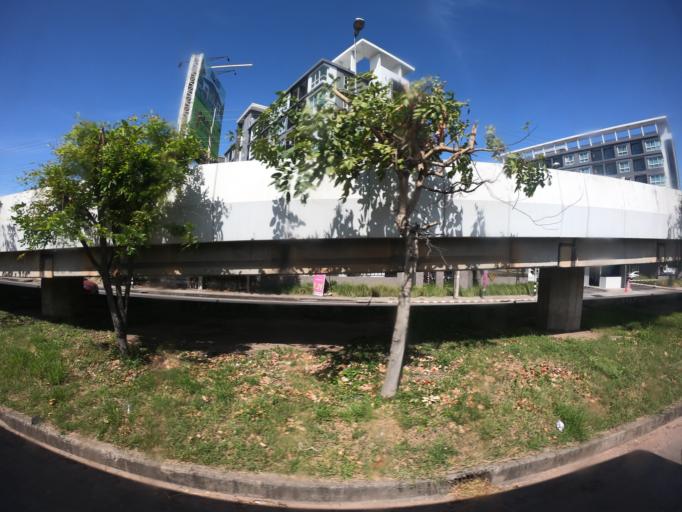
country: TH
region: Nakhon Ratchasima
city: Nakhon Ratchasima
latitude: 15.0029
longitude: 102.1200
